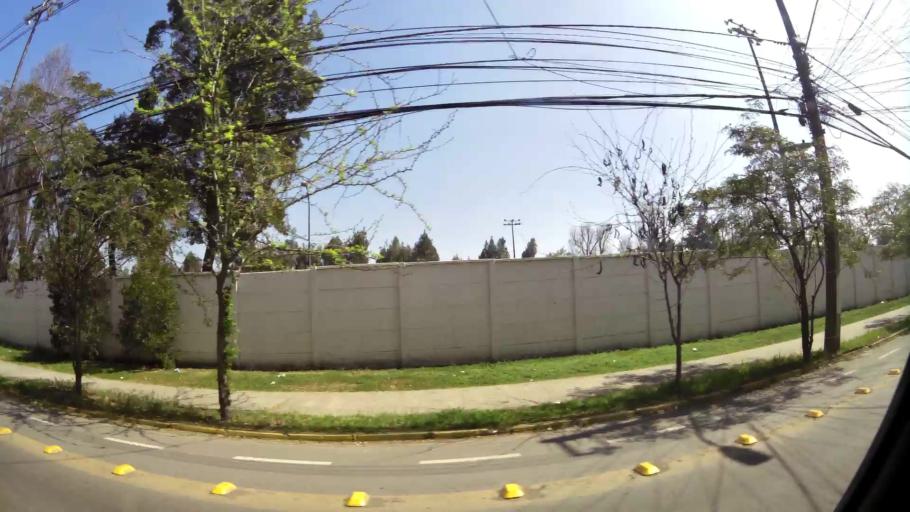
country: CL
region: Santiago Metropolitan
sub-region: Provincia de Santiago
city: Santiago
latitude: -33.4243
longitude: -70.6691
